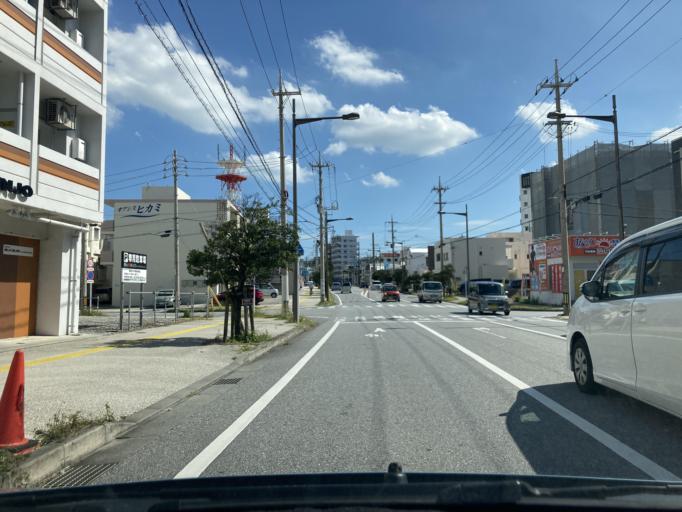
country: JP
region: Okinawa
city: Ginowan
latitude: 26.2702
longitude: 127.7318
